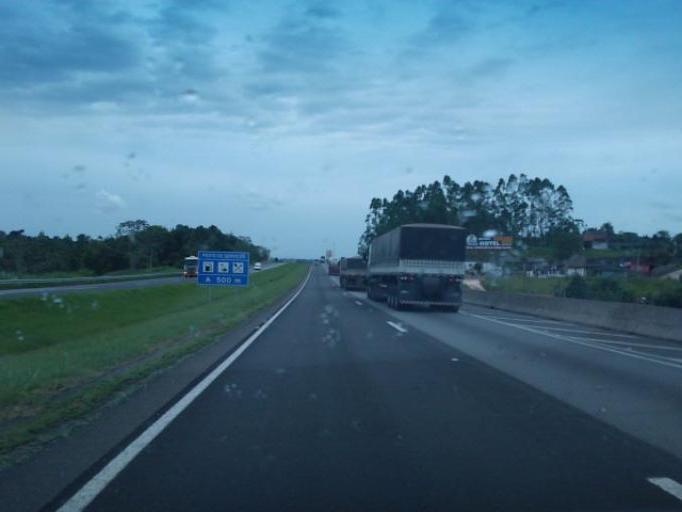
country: BR
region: Sao Paulo
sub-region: Registro
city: Registro
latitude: -24.4697
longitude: -47.8231
